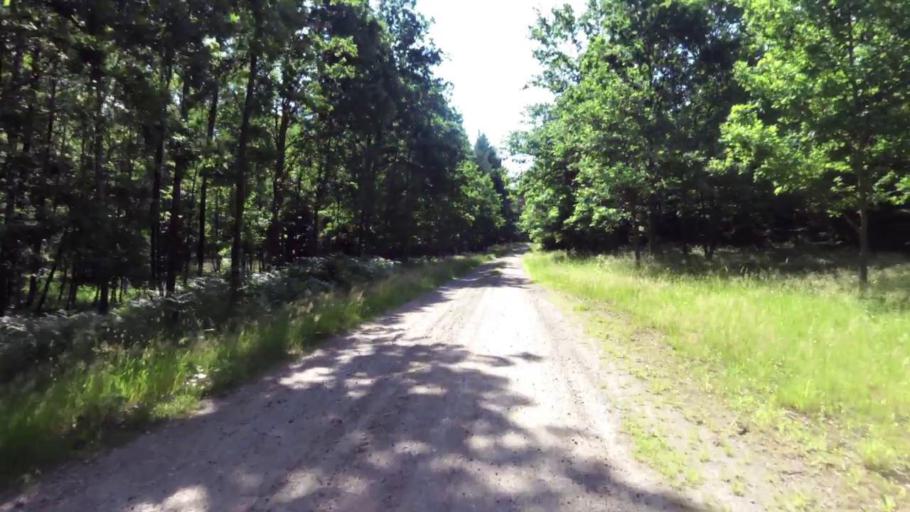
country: PL
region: West Pomeranian Voivodeship
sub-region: Powiat swidwinski
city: Polczyn-Zdroj
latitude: 53.8480
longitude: 16.1431
